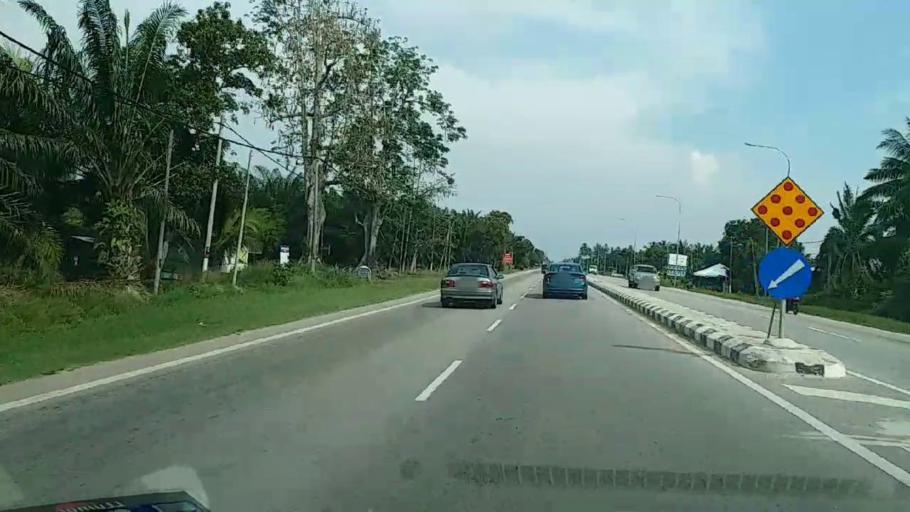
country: MY
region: Selangor
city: Kuala Selangor
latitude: 3.3789
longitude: 101.2348
